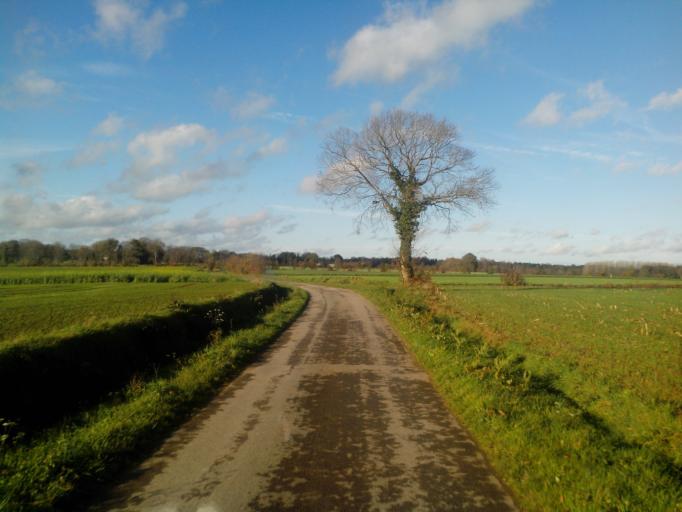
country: FR
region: Brittany
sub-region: Departement du Morbihan
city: Meneac
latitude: 48.1102
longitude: -2.4037
